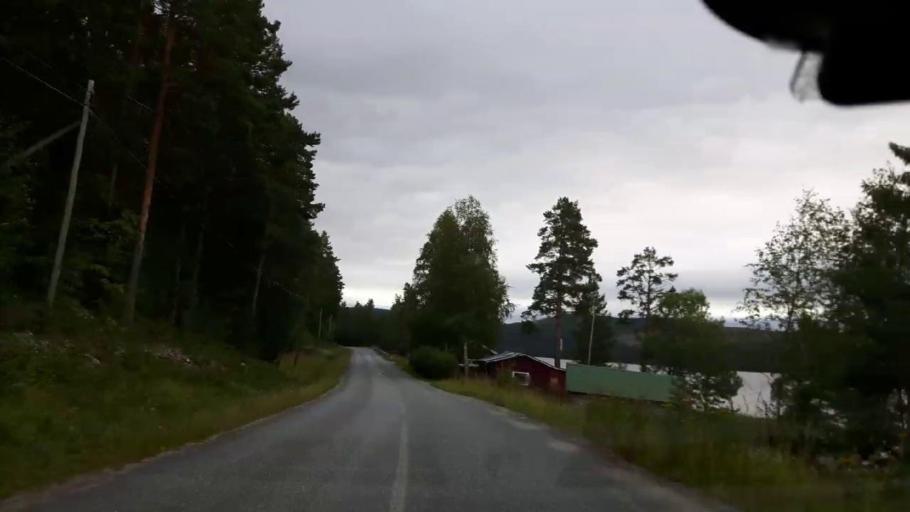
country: SE
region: Jaemtland
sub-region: Braecke Kommun
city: Braecke
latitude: 62.8707
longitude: 15.6154
